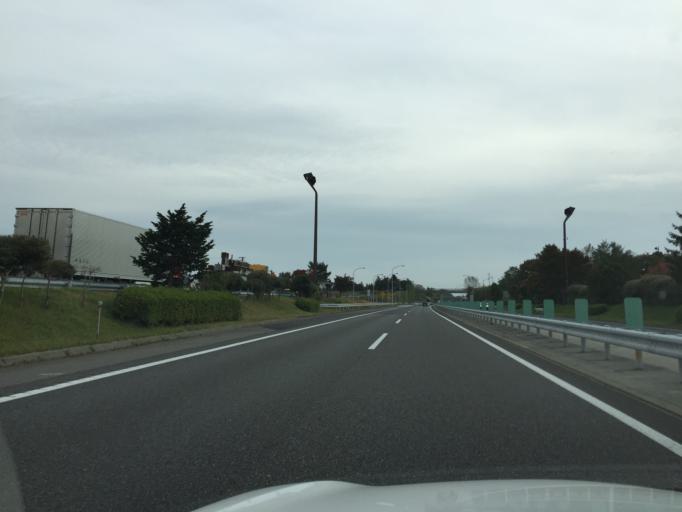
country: JP
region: Fukushima
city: Koriyama
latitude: 37.3536
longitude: 140.3225
